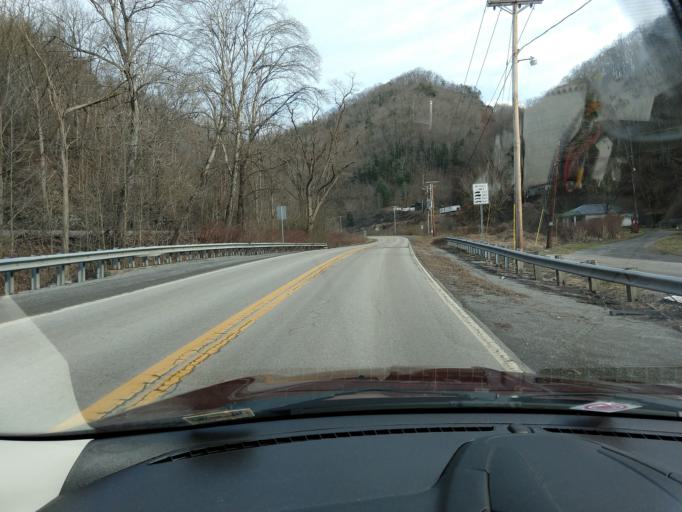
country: US
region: West Virginia
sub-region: McDowell County
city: Welch
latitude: 37.3211
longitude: -81.6942
